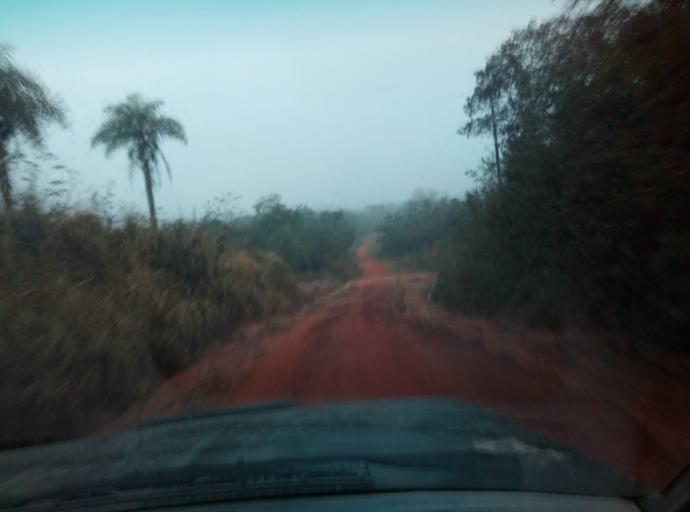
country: PY
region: Caaguazu
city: Doctor Cecilio Baez
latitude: -25.1587
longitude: -56.2559
